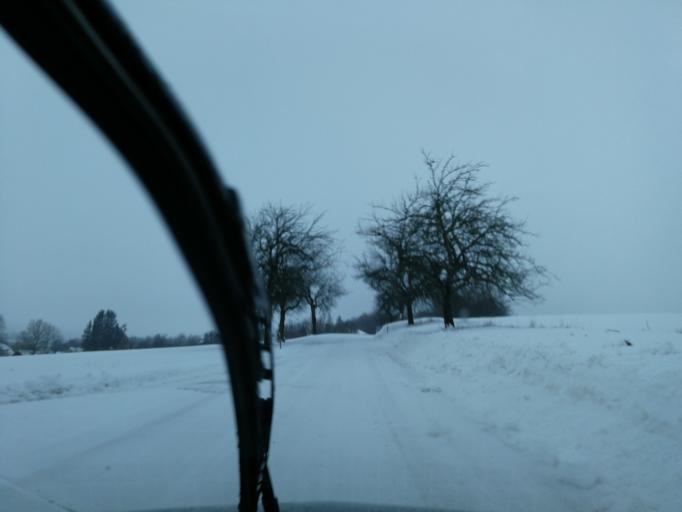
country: CZ
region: Vysocina
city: Heralec
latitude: 49.5272
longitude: 15.4750
